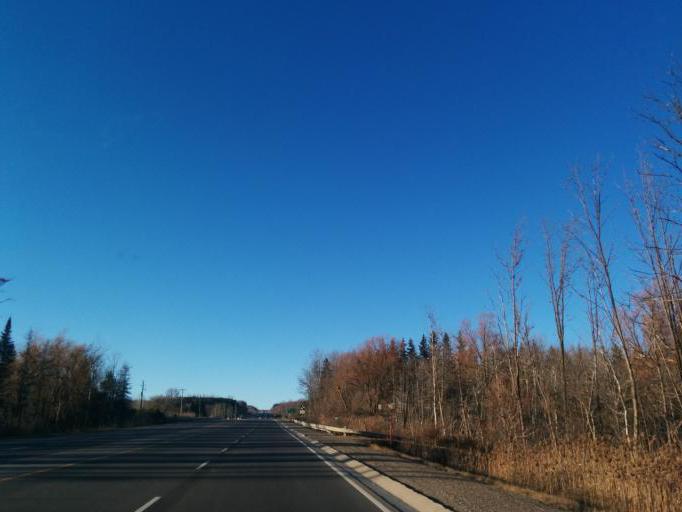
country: CA
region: Ontario
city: Orangeville
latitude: 43.8297
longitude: -79.9543
